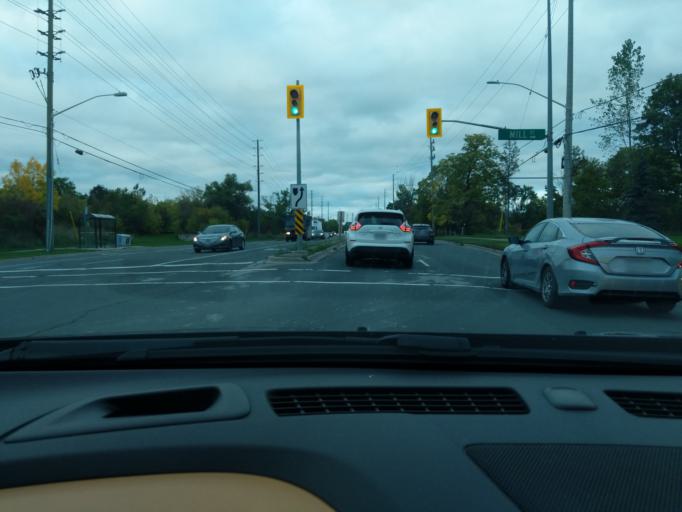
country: CA
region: Ontario
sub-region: York
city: Richmond Hill
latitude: 43.8732
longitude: -79.4645
